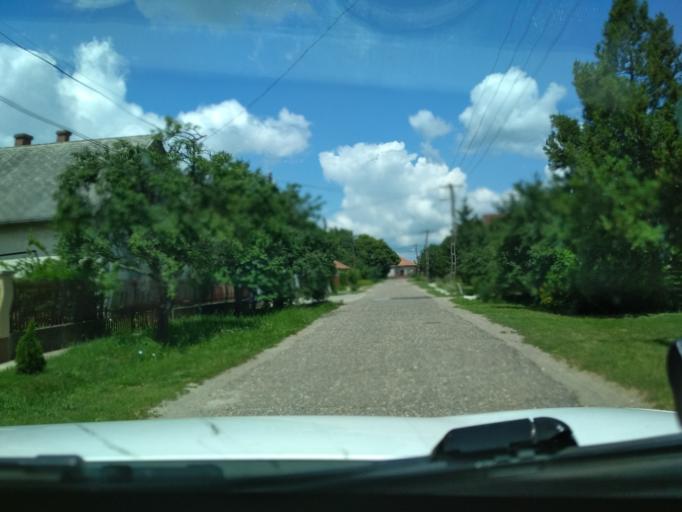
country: HU
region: Jasz-Nagykun-Szolnok
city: Tiszafured
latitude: 47.6117
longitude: 20.7737
